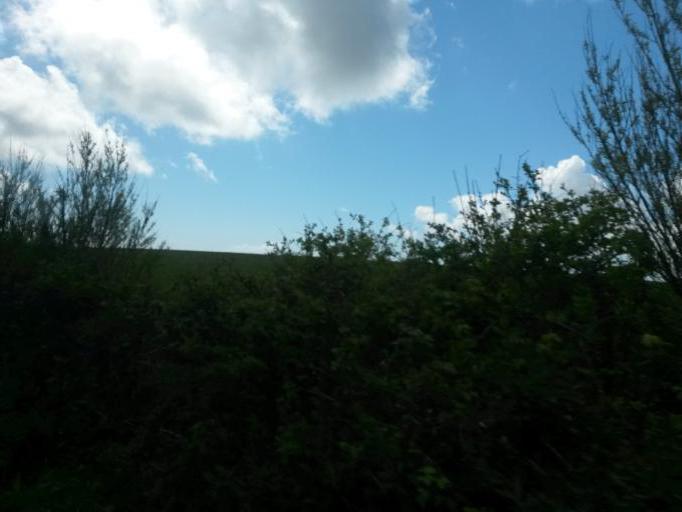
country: IE
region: Munster
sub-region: Waterford
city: Dunmore East
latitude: 52.2064
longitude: -6.8975
